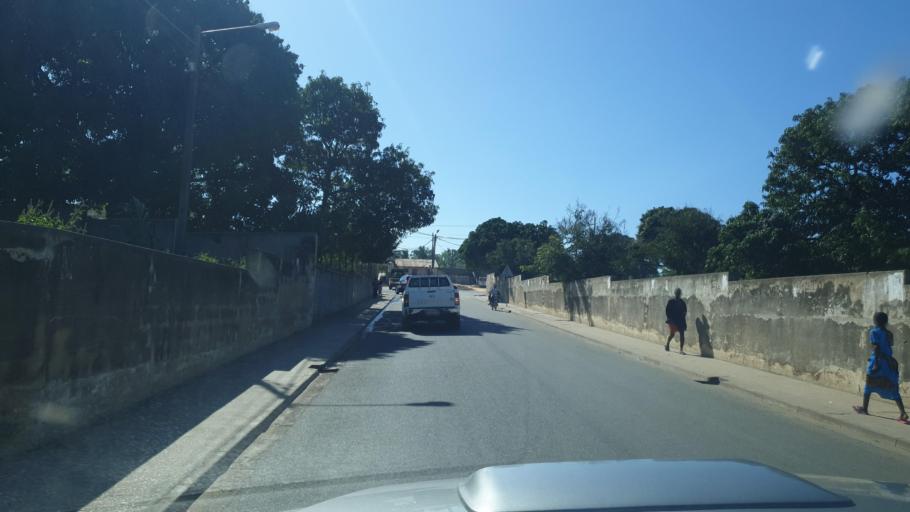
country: MZ
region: Nampula
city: Nacala
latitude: -14.5385
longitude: 40.6814
